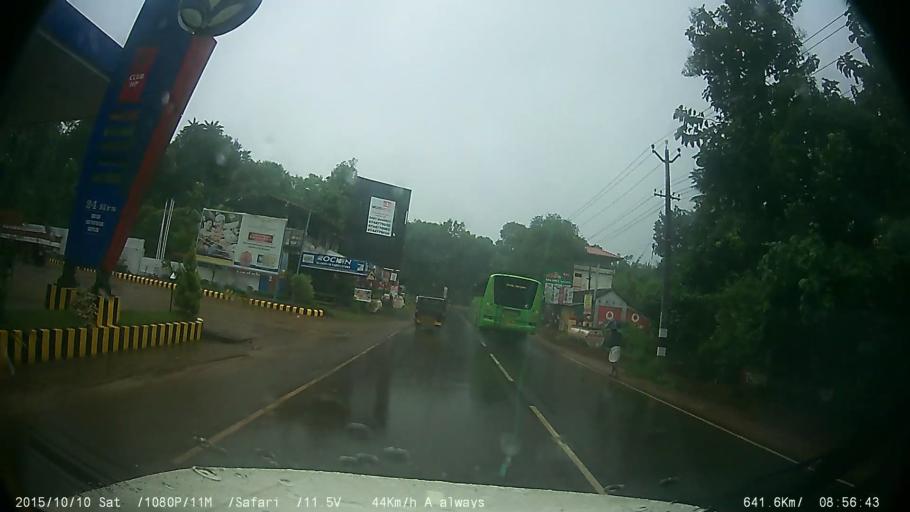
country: IN
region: Kerala
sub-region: Kottayam
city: Palackattumala
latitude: 9.6930
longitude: 76.5519
